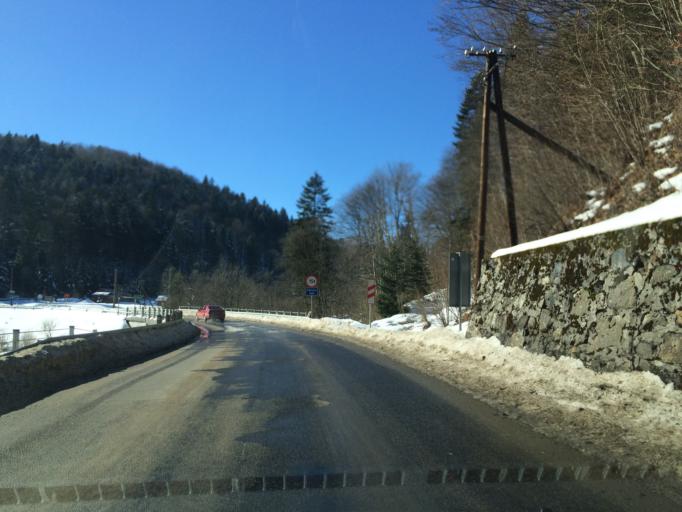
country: PL
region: Subcarpathian Voivodeship
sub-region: Powiat leski
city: Cisna
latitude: 49.2058
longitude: 22.3068
